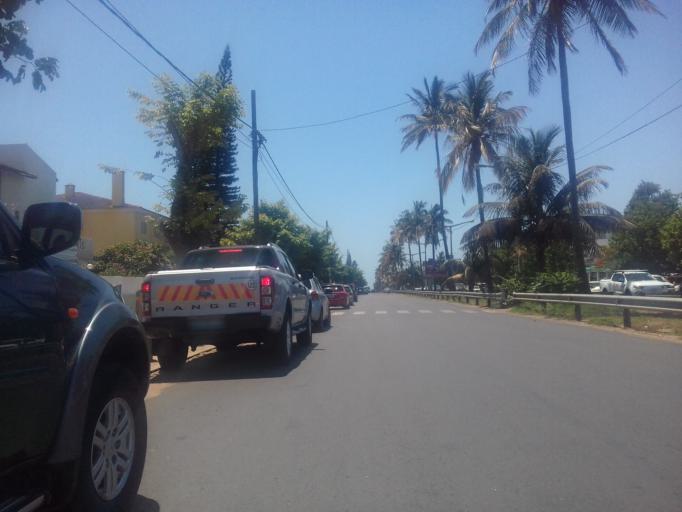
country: MZ
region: Maputo City
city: Maputo
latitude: -25.9548
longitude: 32.5926
